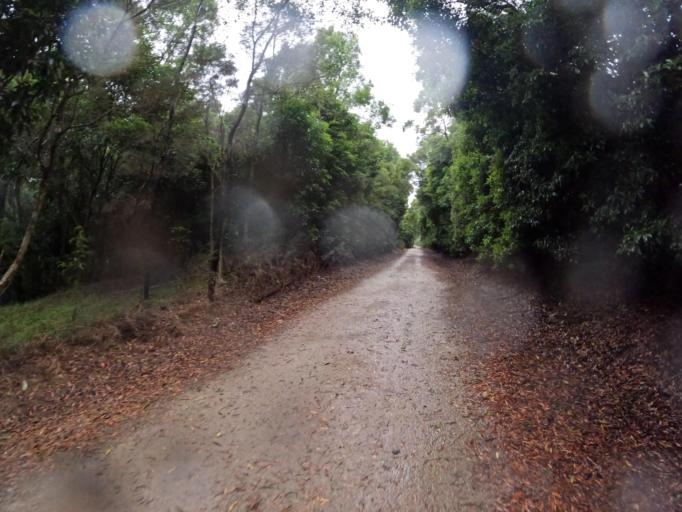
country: AU
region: Victoria
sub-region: Bass Coast
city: North Wonthaggi
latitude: -38.6937
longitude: 146.1129
